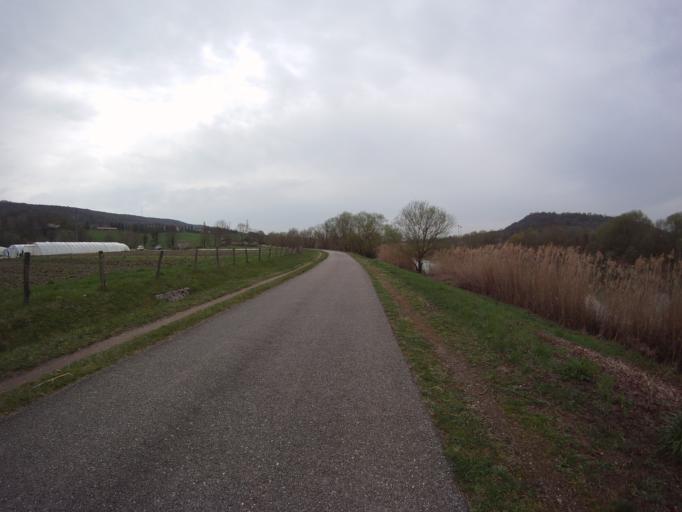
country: FR
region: Lorraine
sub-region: Departement de Meurthe-et-Moselle
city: Champigneulles
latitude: 48.7339
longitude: 6.1722
